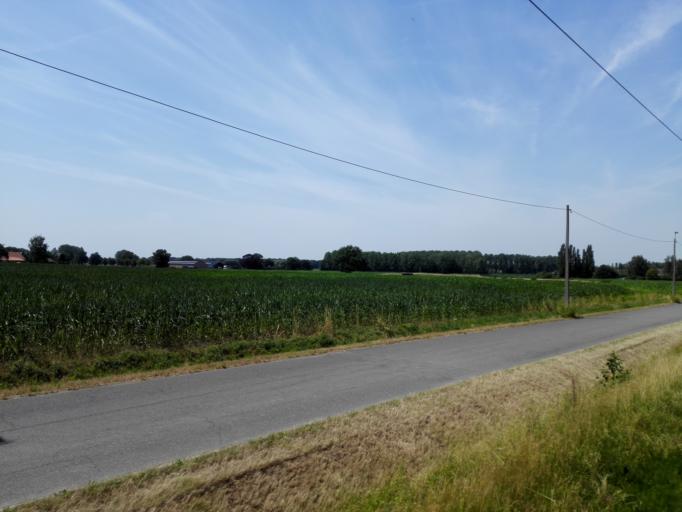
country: BE
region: Flanders
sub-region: Provincie Antwerpen
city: Berlaar
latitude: 51.1207
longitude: 4.6261
